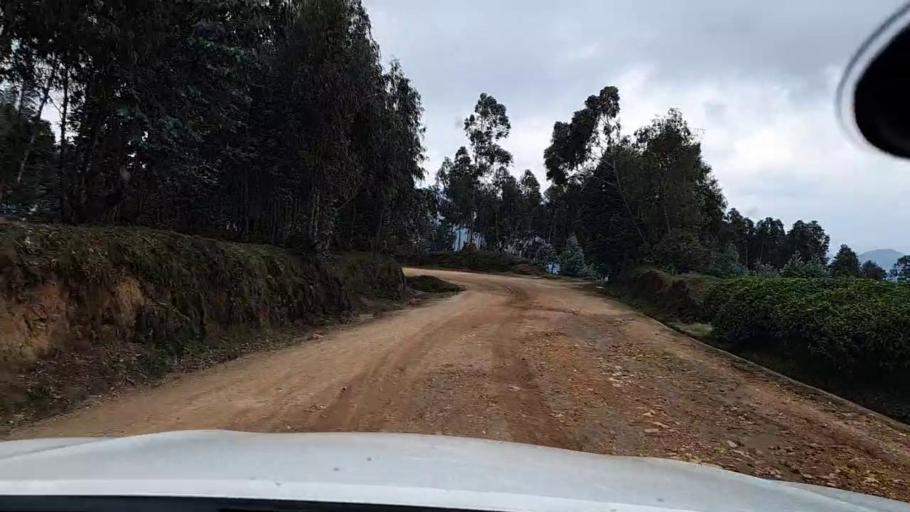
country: RW
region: Western Province
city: Kibuye
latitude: -2.2473
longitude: 29.3439
